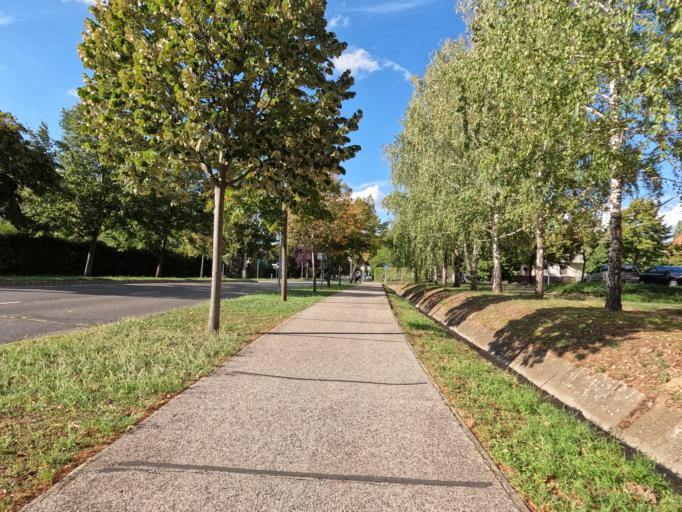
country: HU
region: Tolna
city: Paks
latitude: 46.6131
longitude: 18.8370
